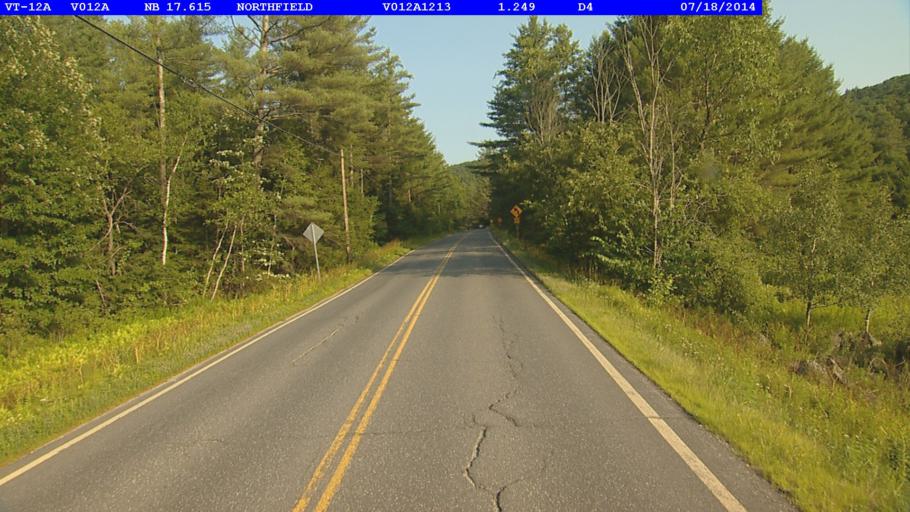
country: US
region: Vermont
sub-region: Washington County
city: Northfield
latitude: 44.1161
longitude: -72.7027
